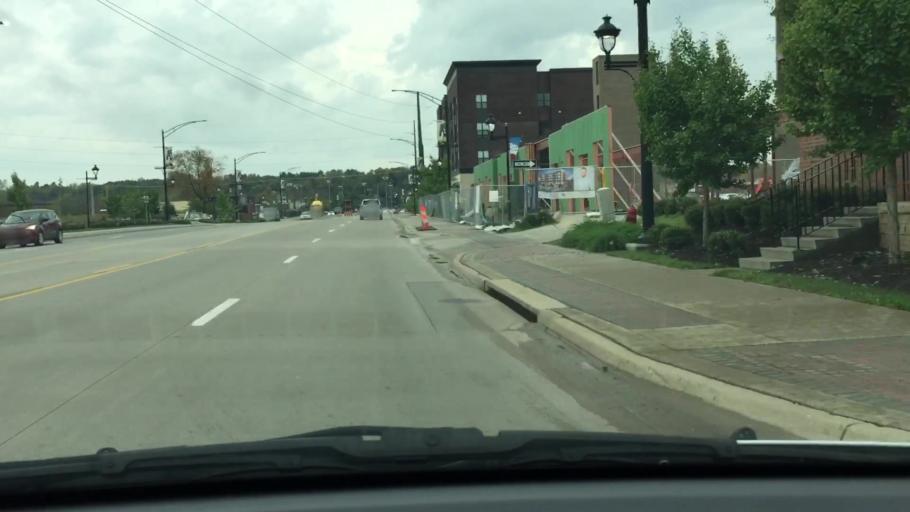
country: US
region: Iowa
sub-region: Johnson County
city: Coralville
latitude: 41.6727
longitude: -91.5656
